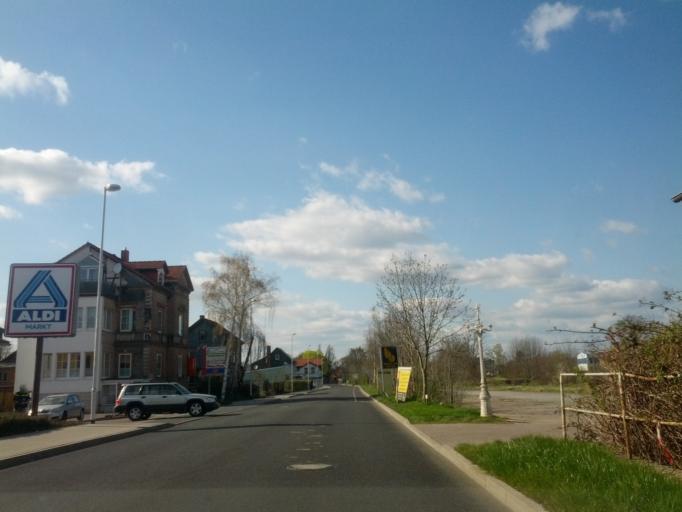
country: DE
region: Thuringia
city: Waltershausen
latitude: 50.8976
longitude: 10.5657
